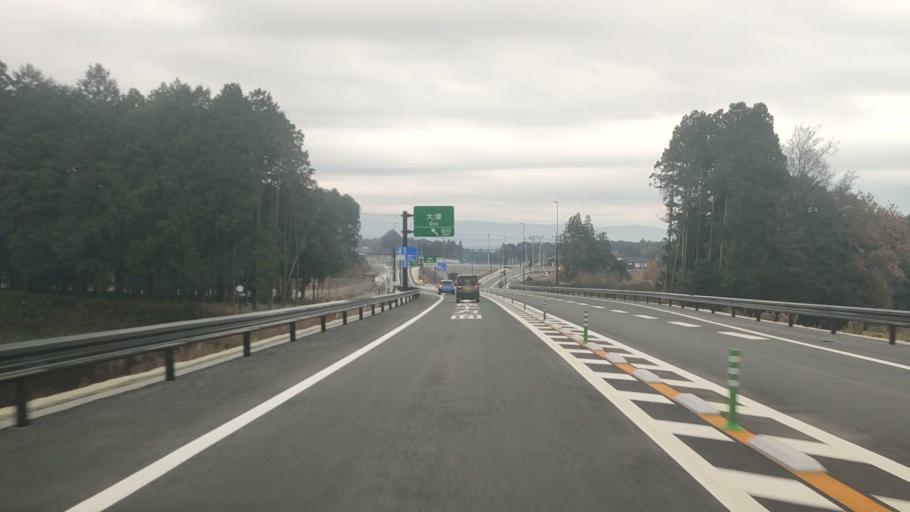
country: JP
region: Kumamoto
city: Ozu
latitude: 32.8932
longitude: 130.8961
